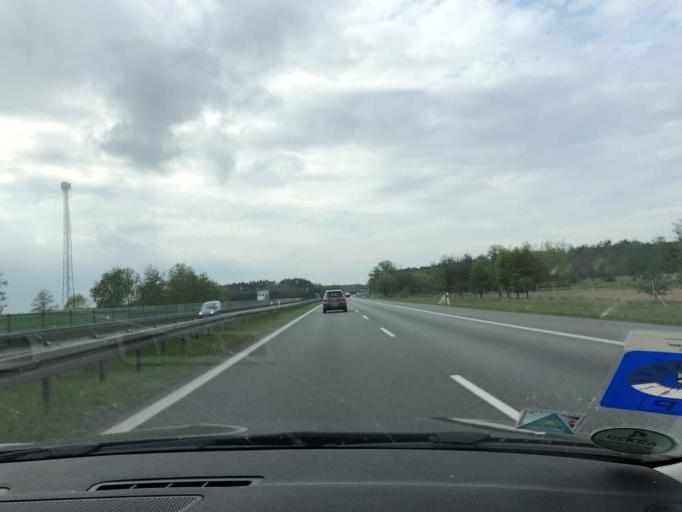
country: PL
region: Opole Voivodeship
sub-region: Powiat opolski
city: Niemodlin
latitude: 50.6800
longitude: 17.6482
